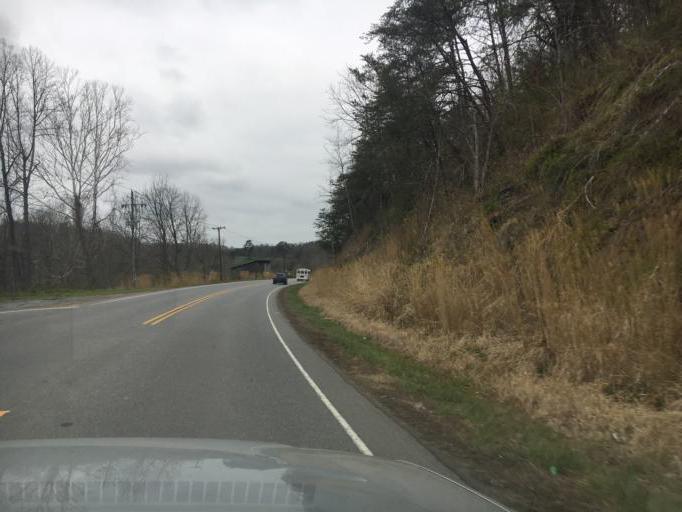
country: US
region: North Carolina
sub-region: Madison County
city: Mars Hill
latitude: 35.7813
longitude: -82.4796
